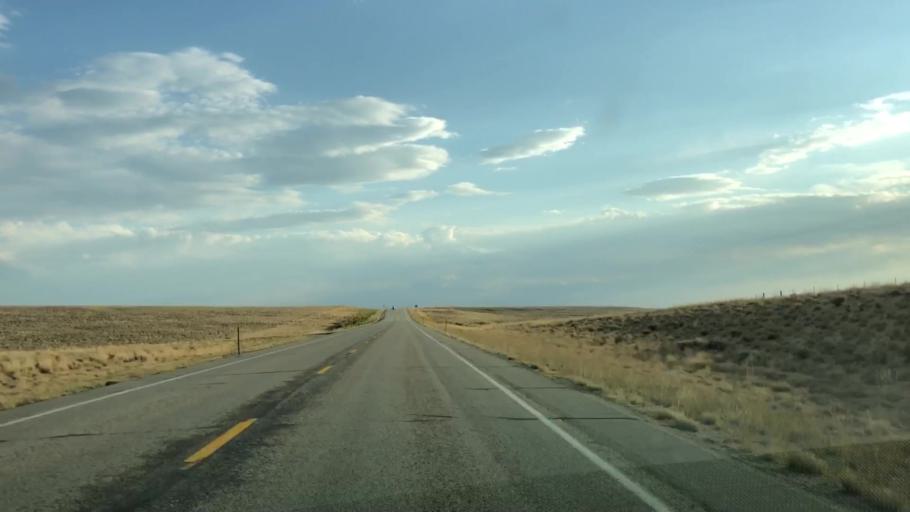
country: US
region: Wyoming
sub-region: Sweetwater County
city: North Rock Springs
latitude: 42.2063
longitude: -109.4752
